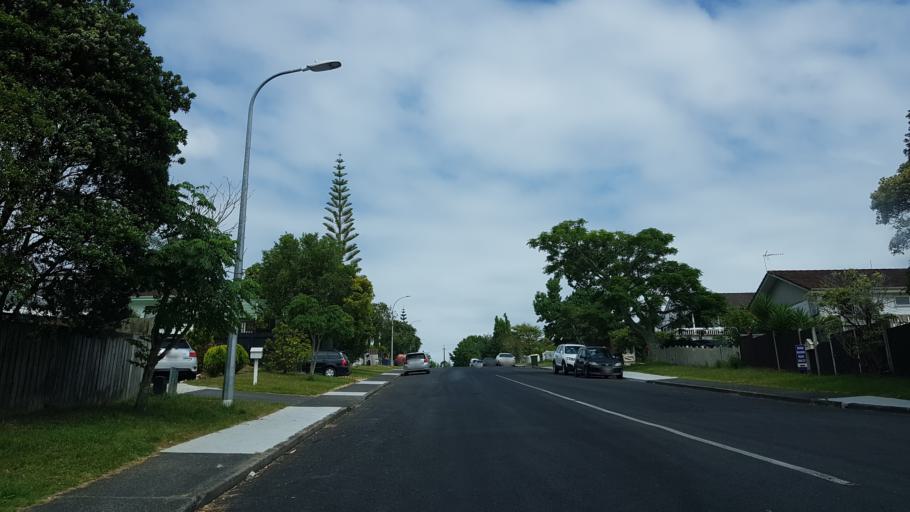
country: NZ
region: Auckland
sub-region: Auckland
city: North Shore
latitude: -36.7738
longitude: 174.7025
